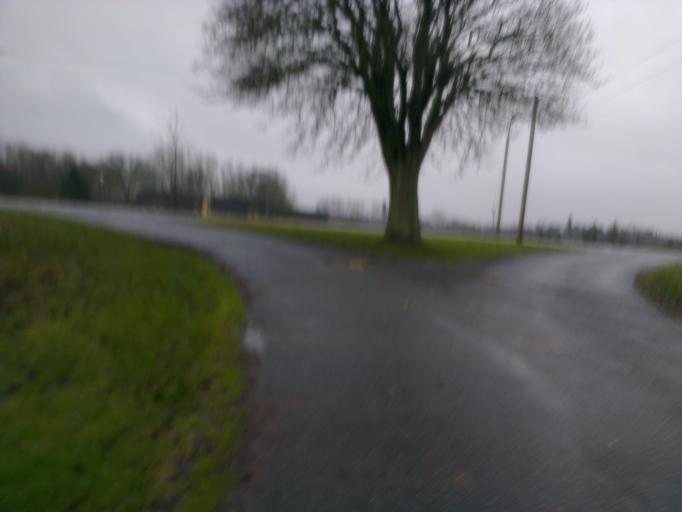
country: DK
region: Capital Region
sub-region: Frederikssund Kommune
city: Jaegerspris
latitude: 55.8176
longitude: 12.0019
